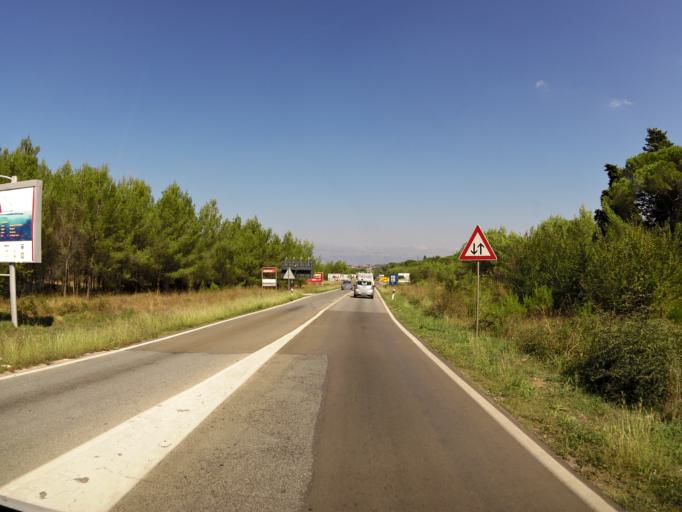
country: HR
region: Zadarska
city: Zadar
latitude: 44.1246
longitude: 15.2825
